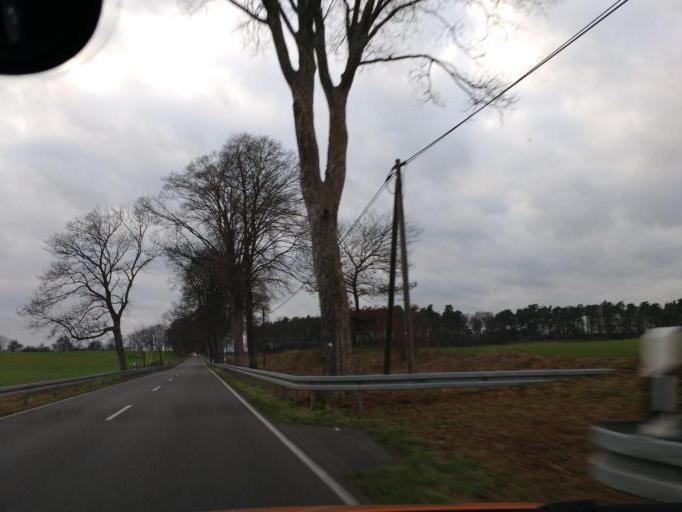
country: DE
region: Brandenburg
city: Protzel
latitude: 52.6516
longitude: 14.0219
